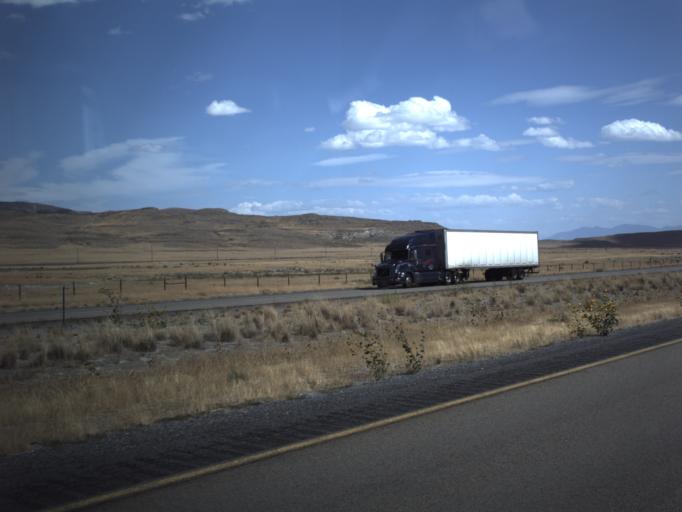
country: US
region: Utah
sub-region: Tooele County
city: Grantsville
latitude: 40.8027
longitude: -112.8546
